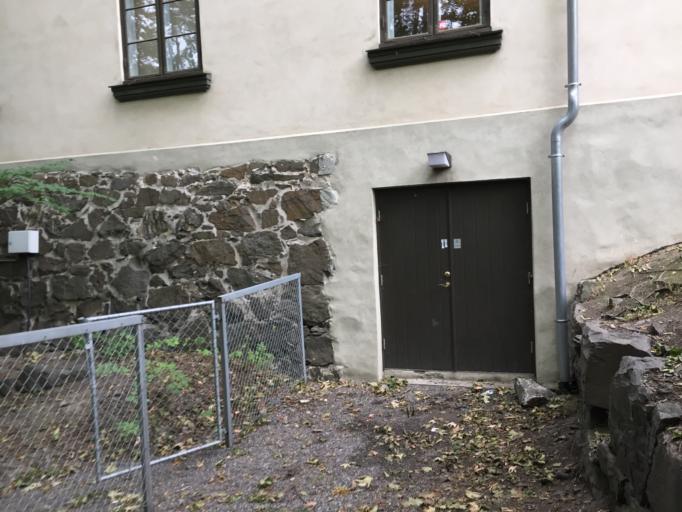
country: NO
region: Oslo
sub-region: Oslo
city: Oslo
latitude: 59.9128
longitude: 10.7182
